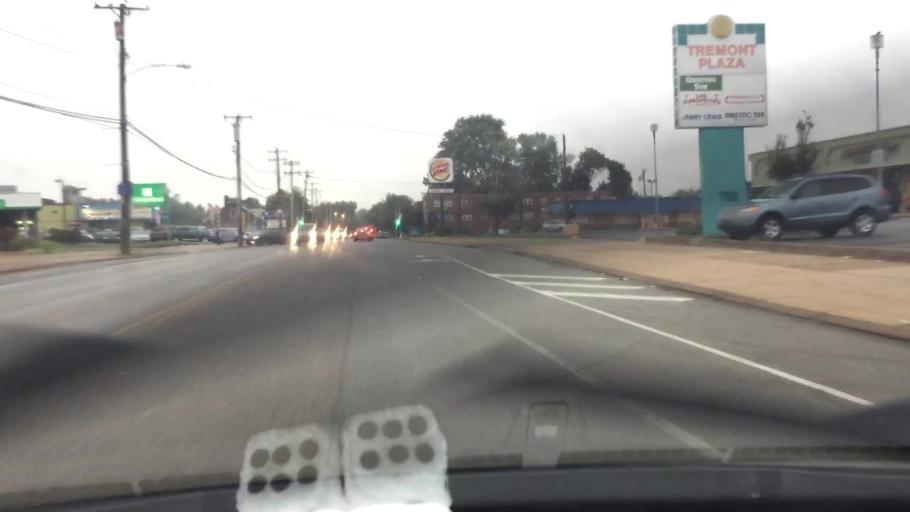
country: US
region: Pennsylvania
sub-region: Montgomery County
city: Rockledge
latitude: 40.0733
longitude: -75.0340
